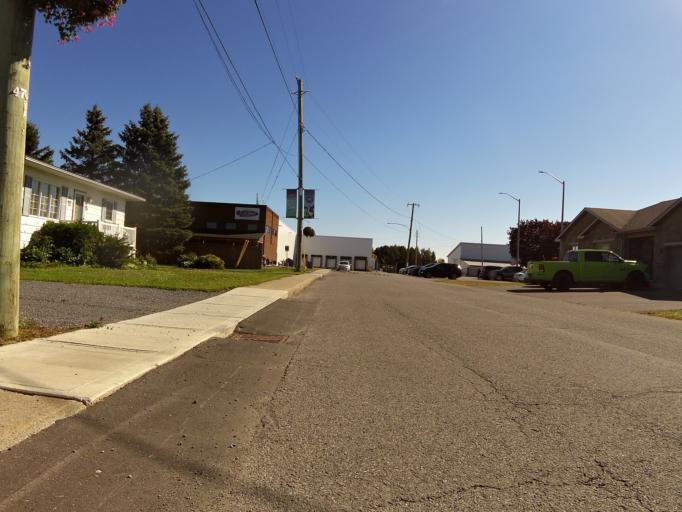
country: CA
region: Ontario
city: Casselman
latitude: 45.2539
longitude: -75.1227
